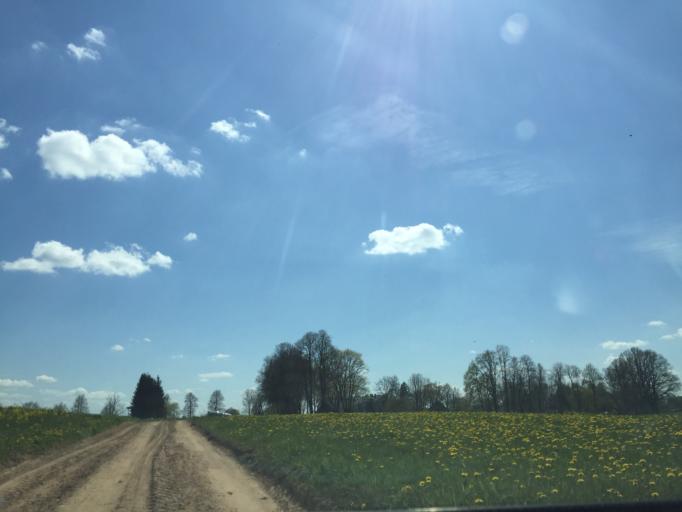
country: LV
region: Vecumnieki
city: Vecumnieki
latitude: 56.4658
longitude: 24.6173
